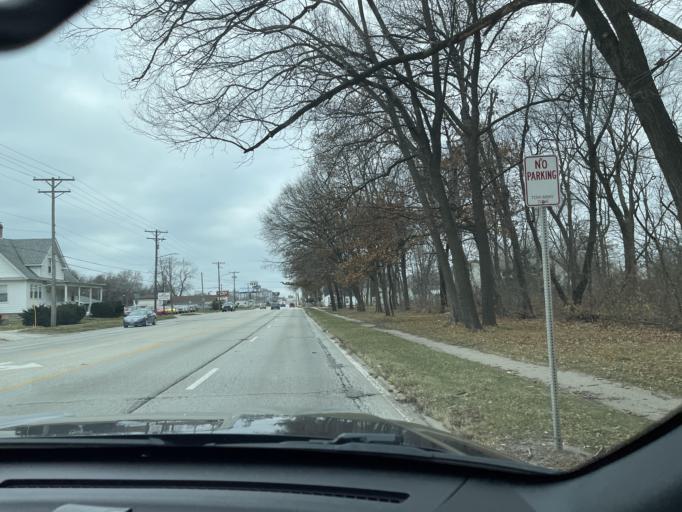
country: US
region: Illinois
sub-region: Sangamon County
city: Grandview
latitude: 39.8021
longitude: -89.6188
